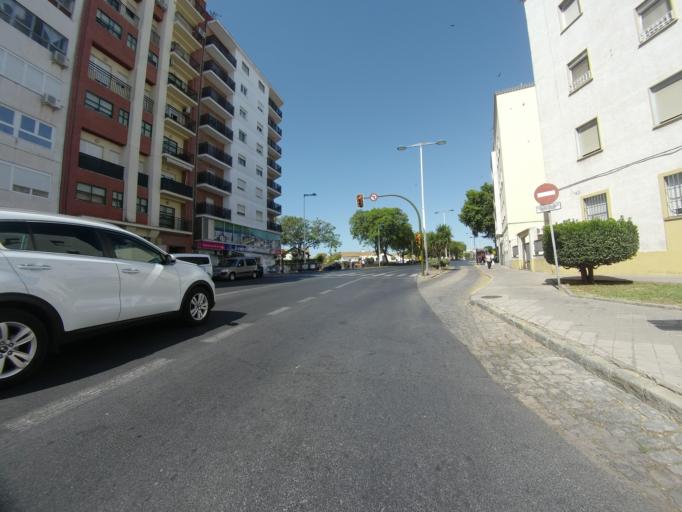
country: ES
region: Andalusia
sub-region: Provincia de Huelva
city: Huelva
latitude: 37.2566
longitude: -6.9376
